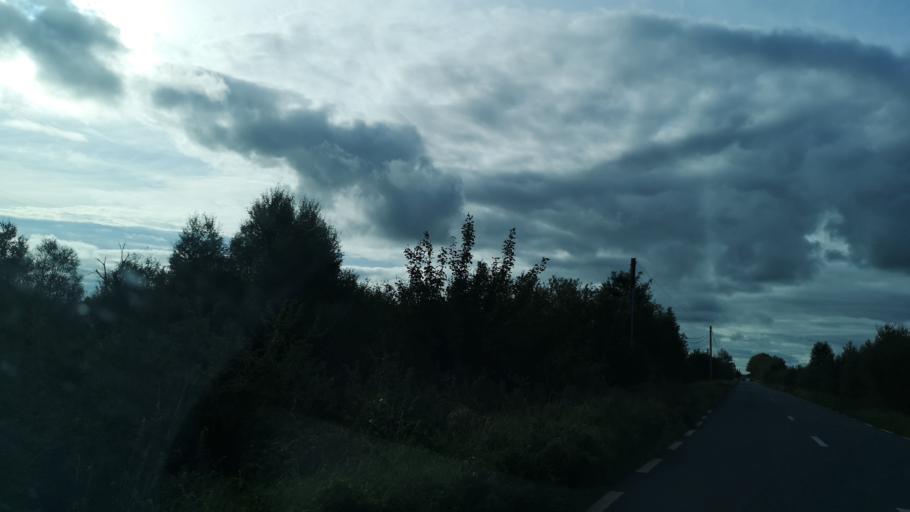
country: IE
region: Leinster
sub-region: Uibh Fhaili
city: Banagher
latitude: 53.2853
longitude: -8.0774
